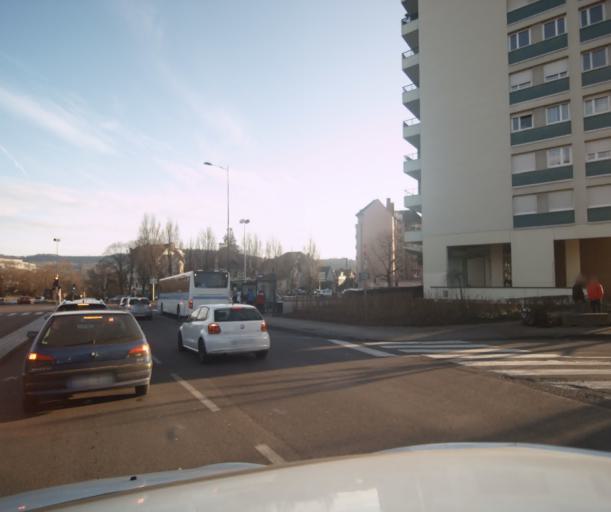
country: FR
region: Franche-Comte
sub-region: Departement du Doubs
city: Besancon
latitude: 47.2427
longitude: 6.0145
